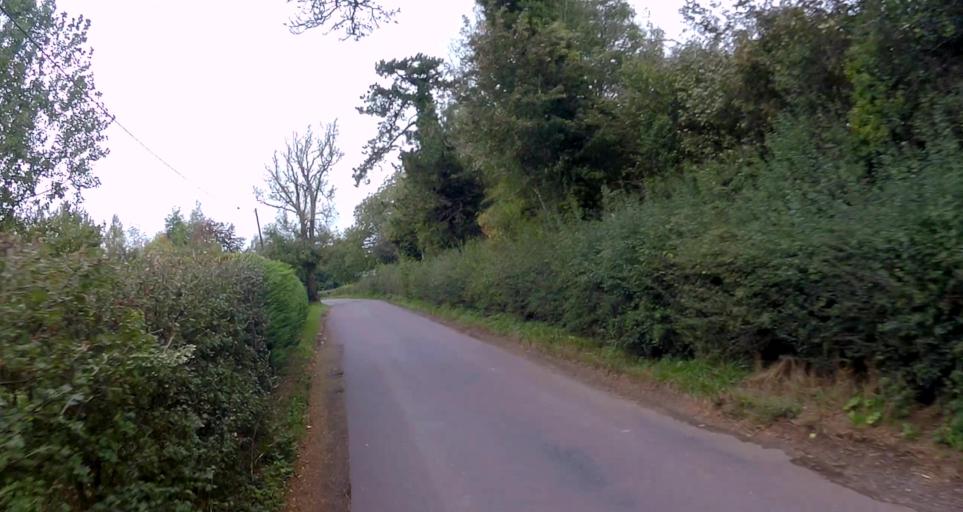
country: GB
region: England
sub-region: Hampshire
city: Four Marks
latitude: 51.1371
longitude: -1.0808
